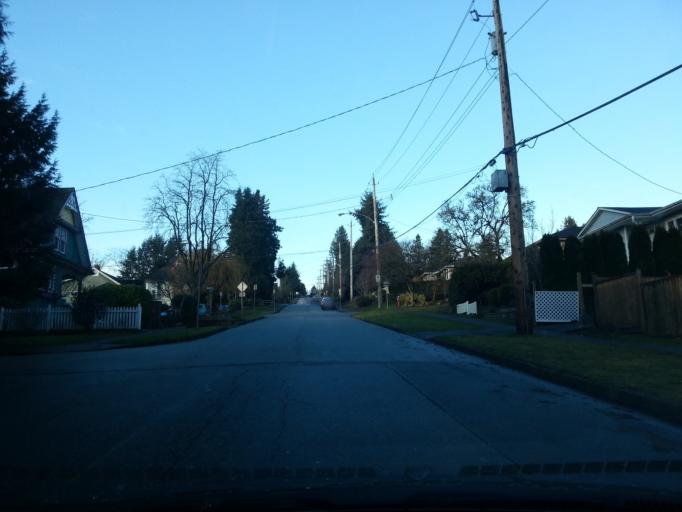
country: CA
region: British Columbia
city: New Westminster
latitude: 49.2279
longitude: -122.8954
